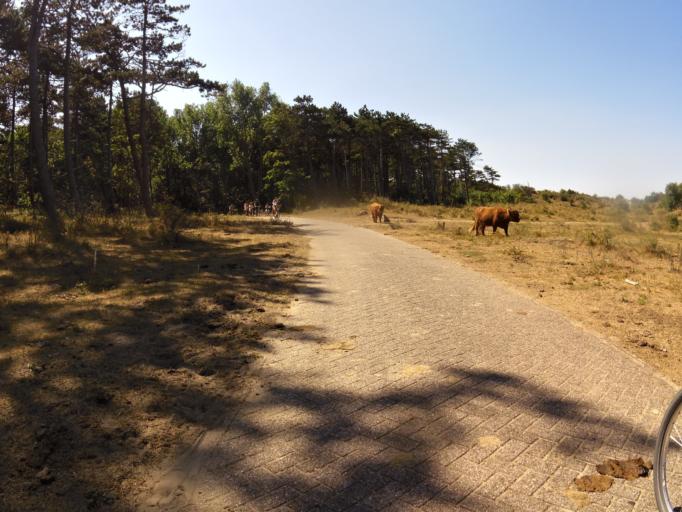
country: NL
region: North Holland
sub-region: Gemeente Beverwijk
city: Beverwijk
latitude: 52.5150
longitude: 4.6145
